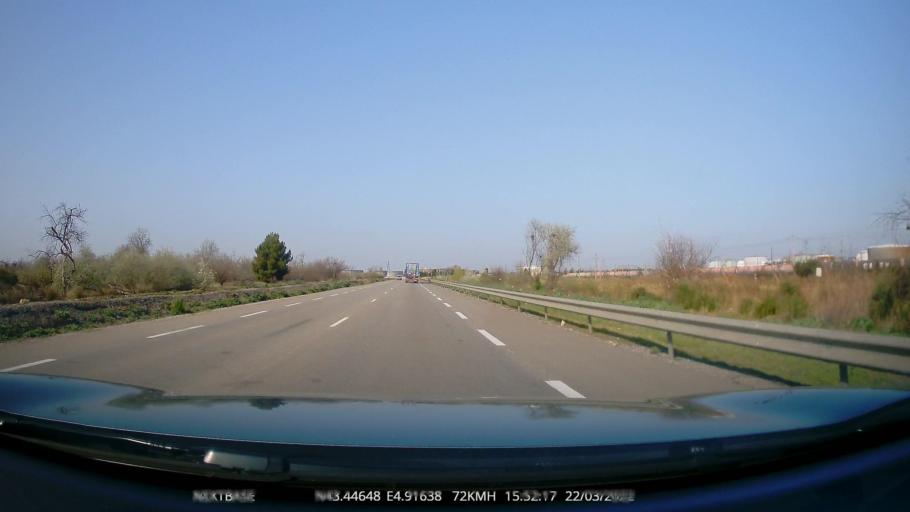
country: FR
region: Provence-Alpes-Cote d'Azur
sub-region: Departement des Bouches-du-Rhone
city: Fos-sur-Mer
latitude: 43.4464
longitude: 4.9162
